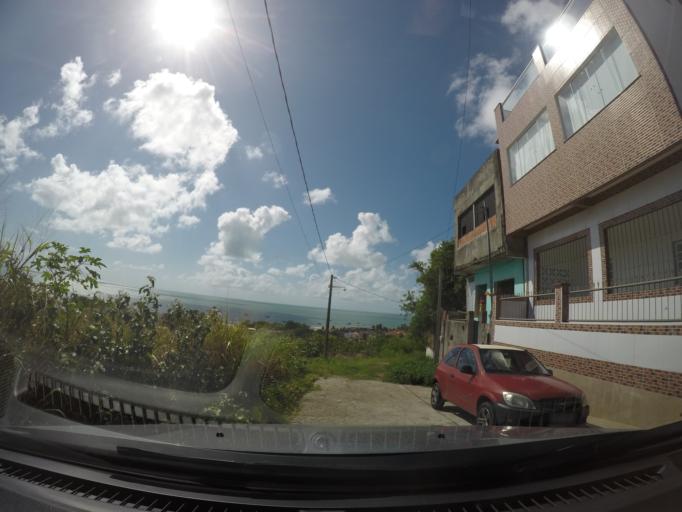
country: BR
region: Paraiba
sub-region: Pitimbu
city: Pitimbu
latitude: -7.4735
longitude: -34.8106
